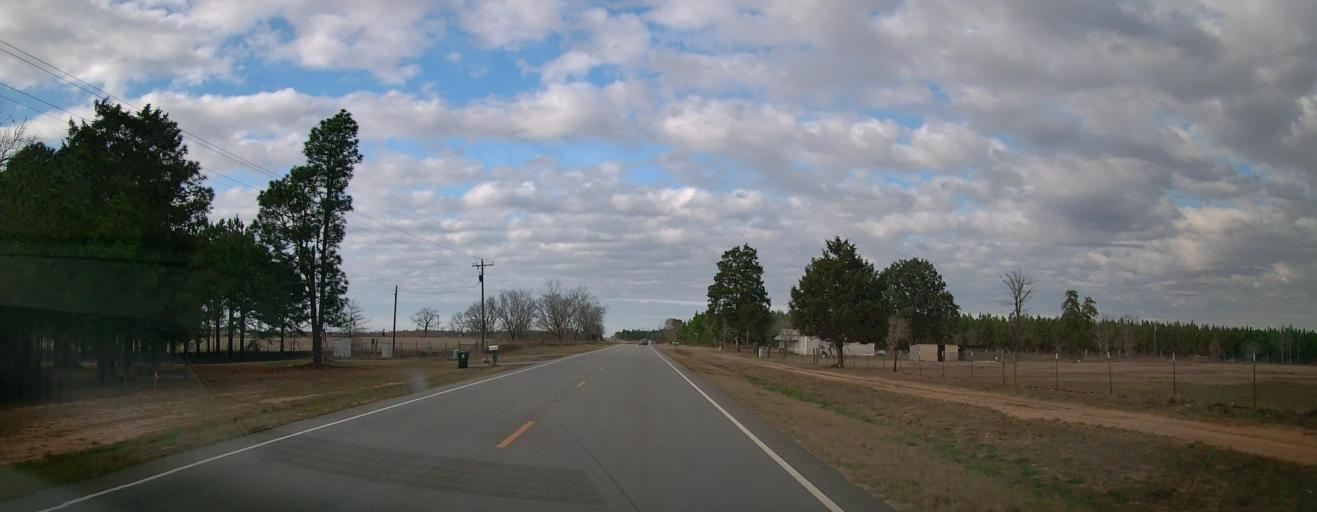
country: US
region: Georgia
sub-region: Marion County
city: Buena Vista
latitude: 32.4641
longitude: -84.5394
